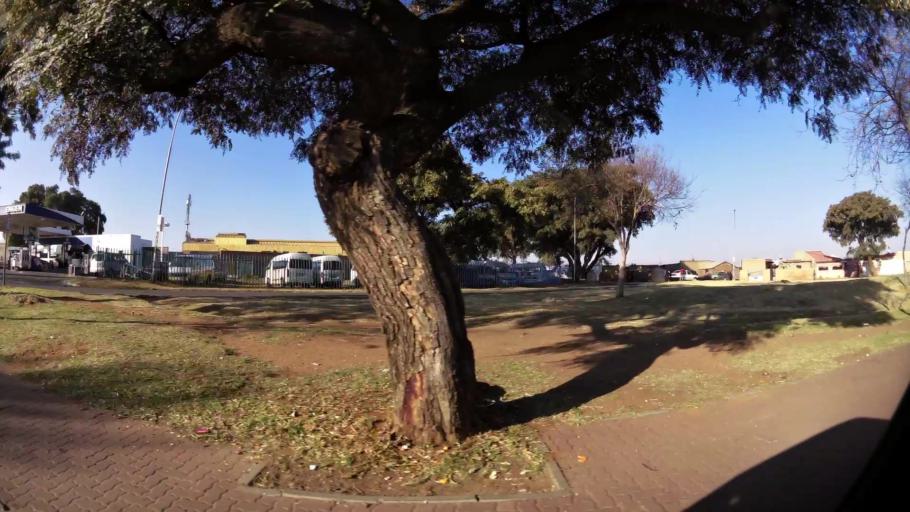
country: ZA
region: Gauteng
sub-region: City of Johannesburg Metropolitan Municipality
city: Soweto
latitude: -26.2428
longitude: 27.9396
